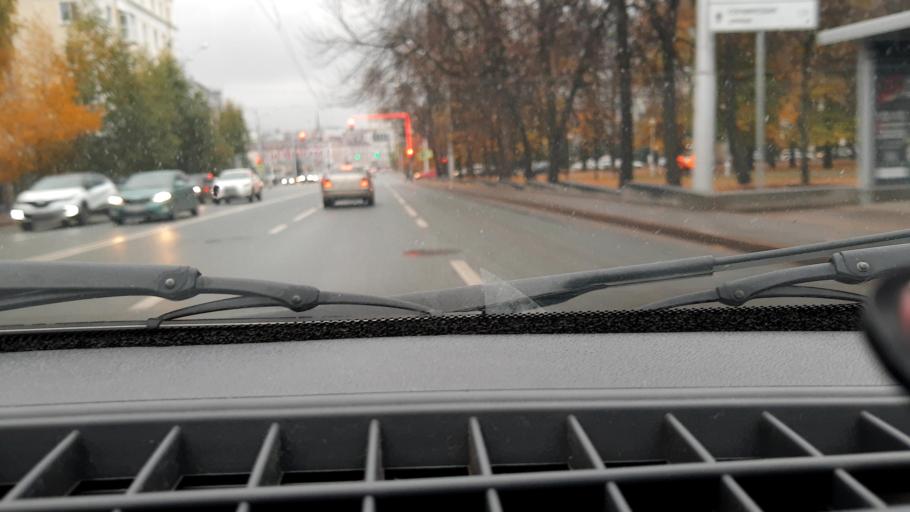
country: RU
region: Bashkortostan
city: Ufa
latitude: 54.7191
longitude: 55.9442
